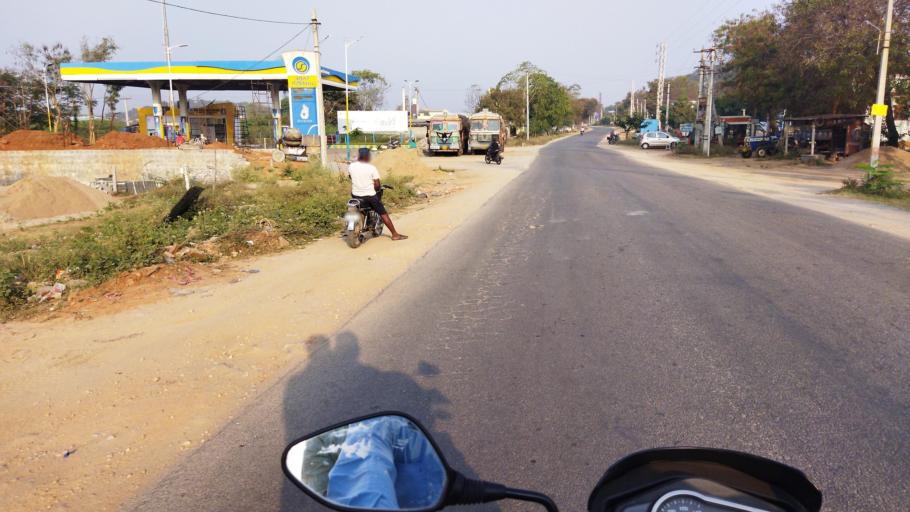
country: IN
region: Telangana
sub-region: Nalgonda
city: Nalgonda
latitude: 17.2363
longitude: 79.1212
